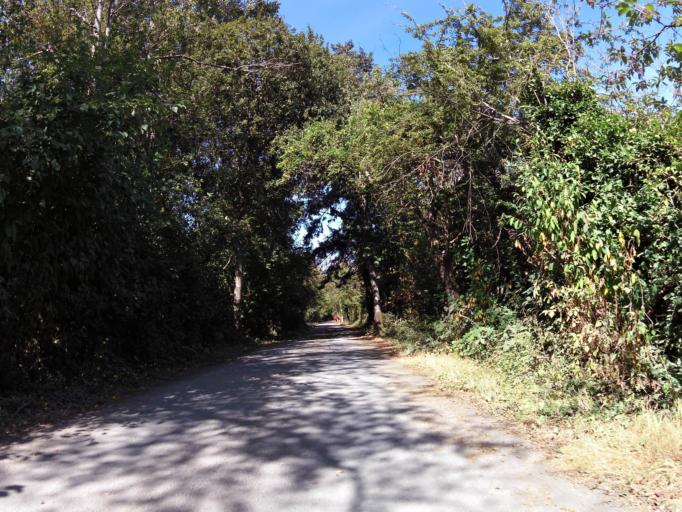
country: CA
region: British Columbia
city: Victoria
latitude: 48.5420
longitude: -123.3825
